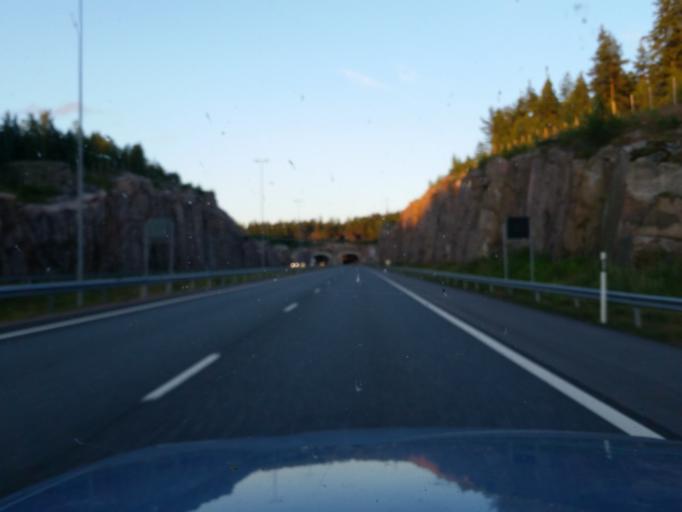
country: FI
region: Varsinais-Suomi
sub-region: Salo
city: Muurla
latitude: 60.3736
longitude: 23.3538
